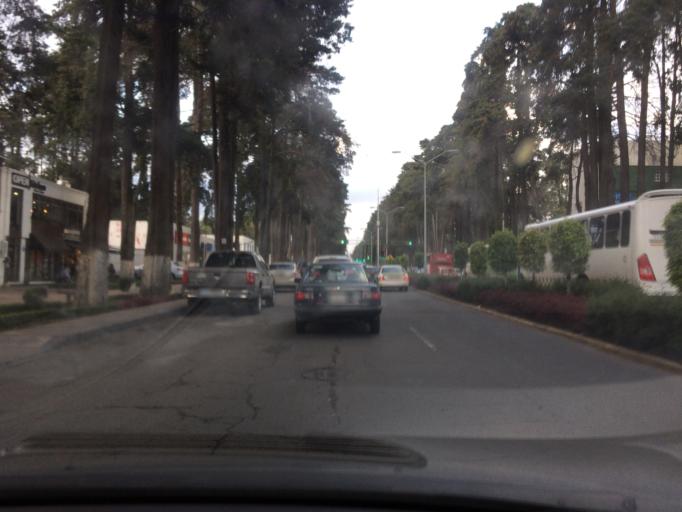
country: MX
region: Mexico
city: Toluca
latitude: 19.2770
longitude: -99.6591
